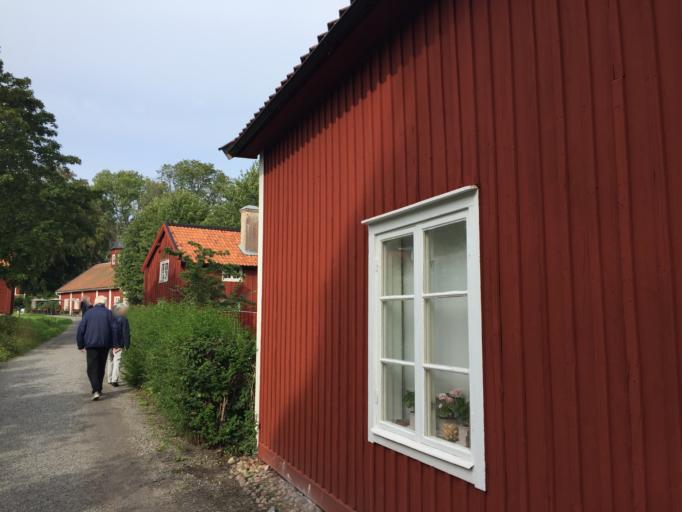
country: SE
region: Stockholm
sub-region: Norrtalje Kommun
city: Norrtalje
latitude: 59.5708
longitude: 18.5489
